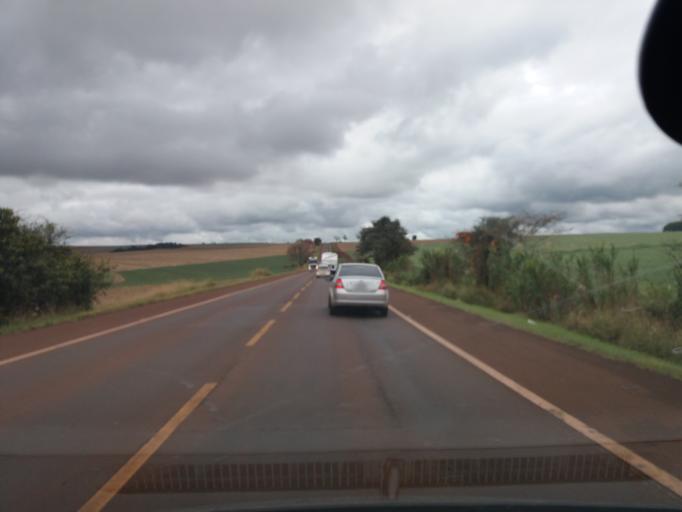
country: BR
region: Parana
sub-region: Corbelia
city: Corbelia
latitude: -24.8461
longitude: -53.3203
